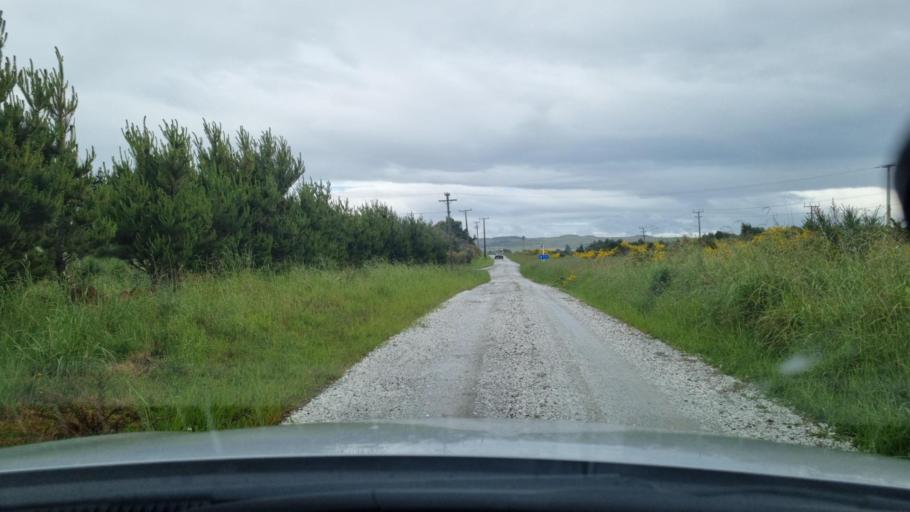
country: NZ
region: Southland
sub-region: Invercargill City
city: Bluff
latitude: -46.5430
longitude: 168.3021
